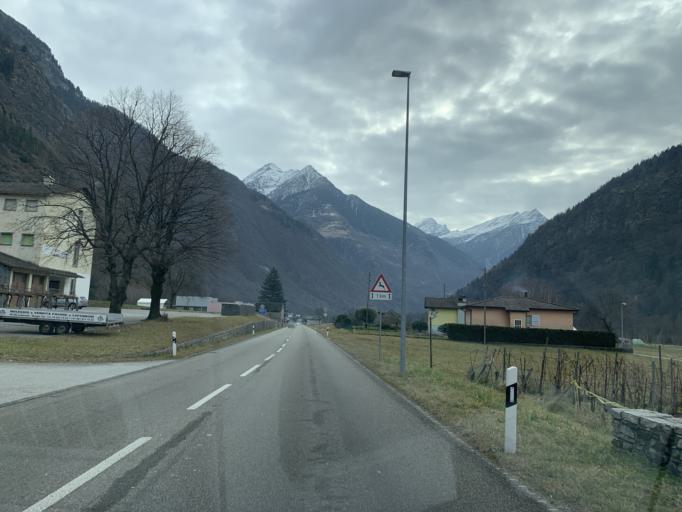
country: CH
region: Ticino
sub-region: Blenio District
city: Acquarossa
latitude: 46.4362
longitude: 8.9573
